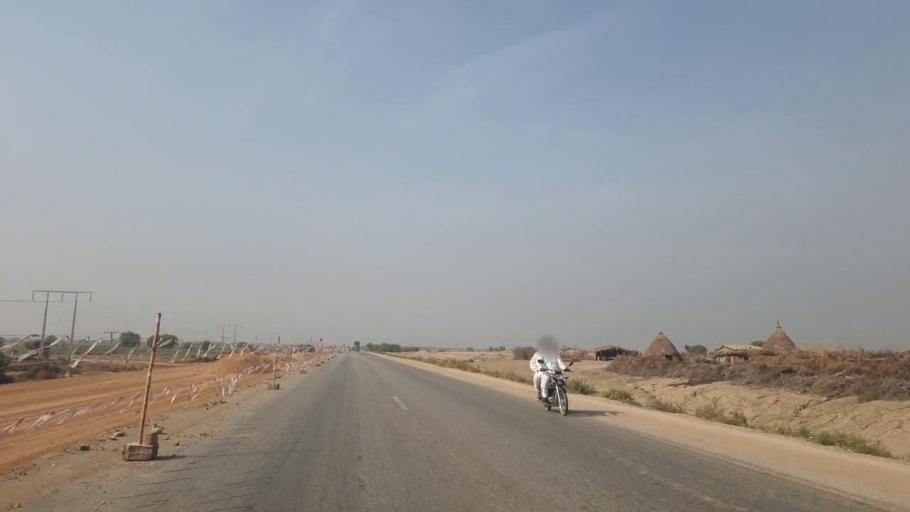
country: PK
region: Sindh
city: Sann
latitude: 26.1436
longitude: 68.0356
